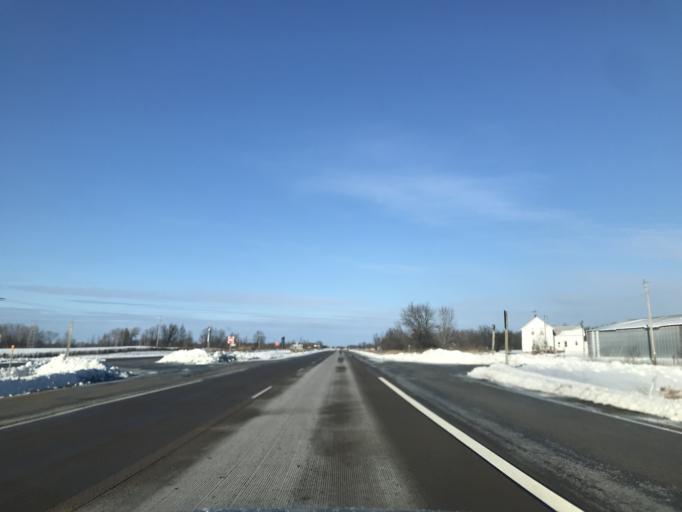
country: US
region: Wisconsin
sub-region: Oconto County
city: Oconto Falls
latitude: 44.9083
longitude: -88.0463
